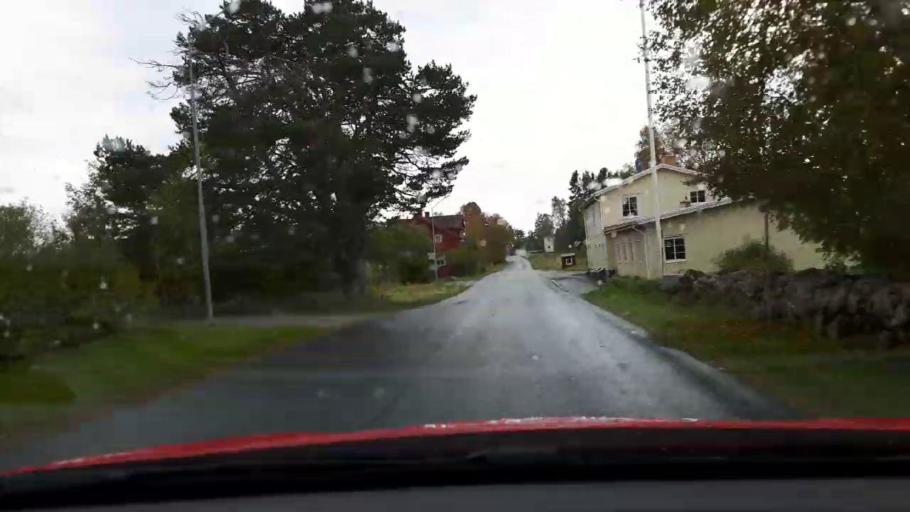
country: SE
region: Jaemtland
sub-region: Bergs Kommun
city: Hoverberg
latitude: 62.9263
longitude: 14.5160
